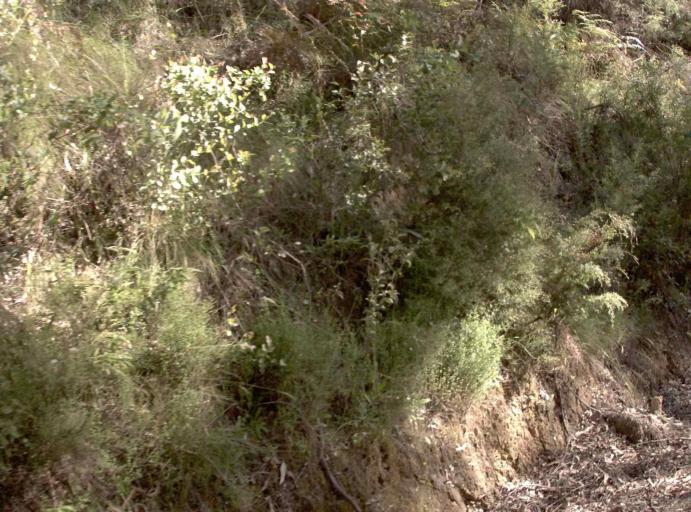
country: AU
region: Victoria
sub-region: East Gippsland
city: Lakes Entrance
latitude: -37.4959
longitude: 148.5541
